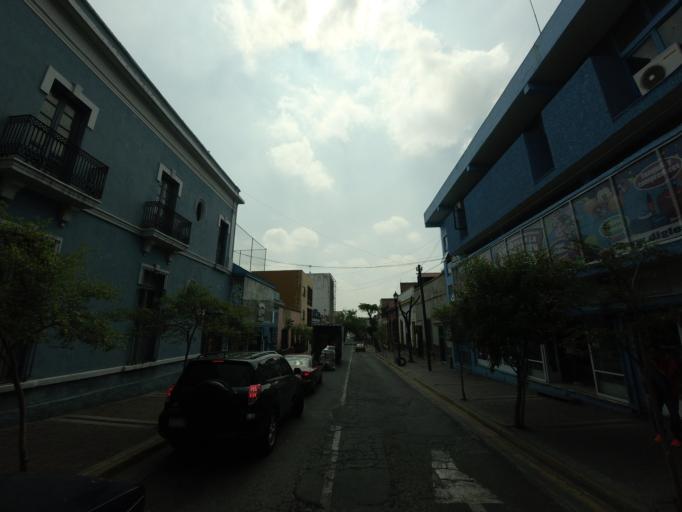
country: MX
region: Jalisco
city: Guadalajara
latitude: 20.6790
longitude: -103.3442
